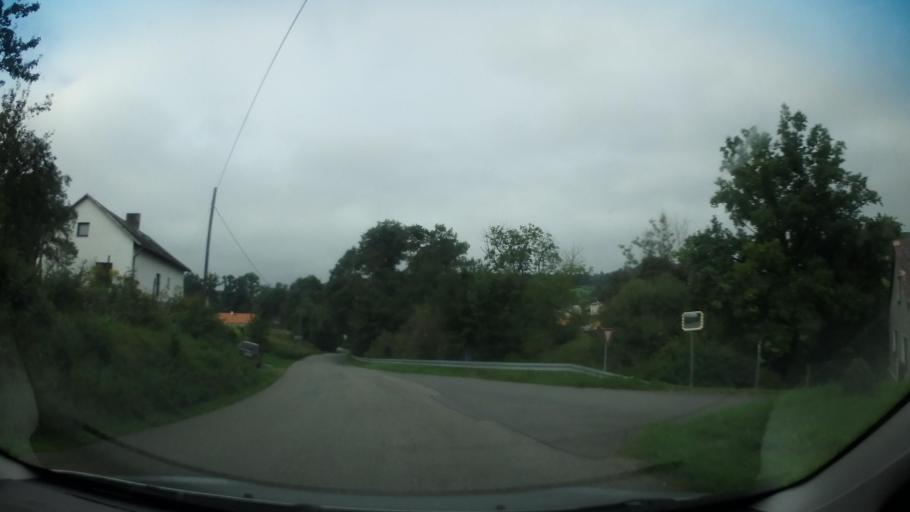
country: CZ
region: Central Bohemia
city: Sedlcany
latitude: 49.7147
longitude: 14.4172
